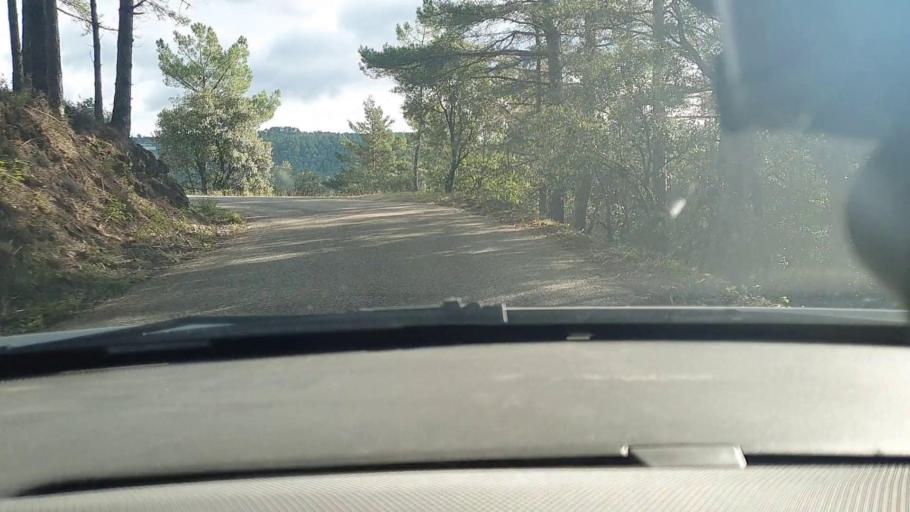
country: FR
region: Languedoc-Roussillon
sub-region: Departement du Gard
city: Besseges
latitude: 44.3226
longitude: 4.0420
